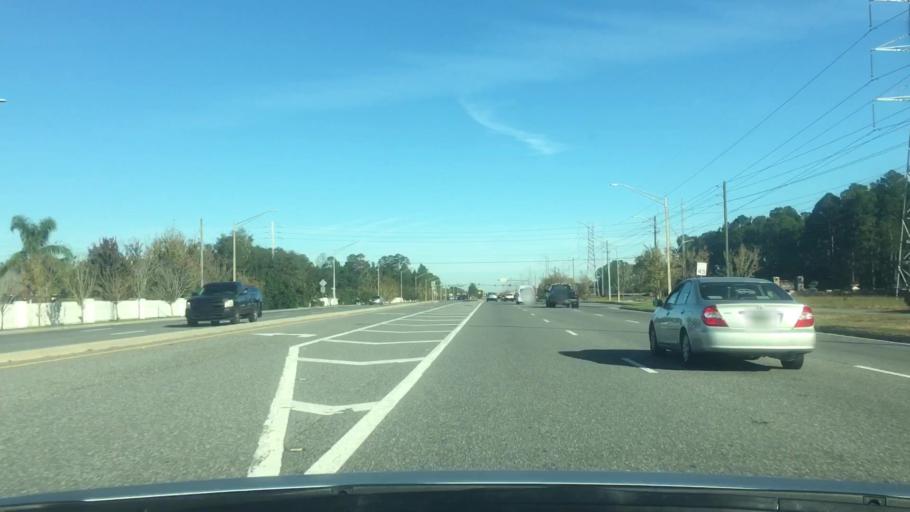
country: US
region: Florida
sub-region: Duval County
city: Neptune Beach
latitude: 30.3008
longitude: -81.4890
